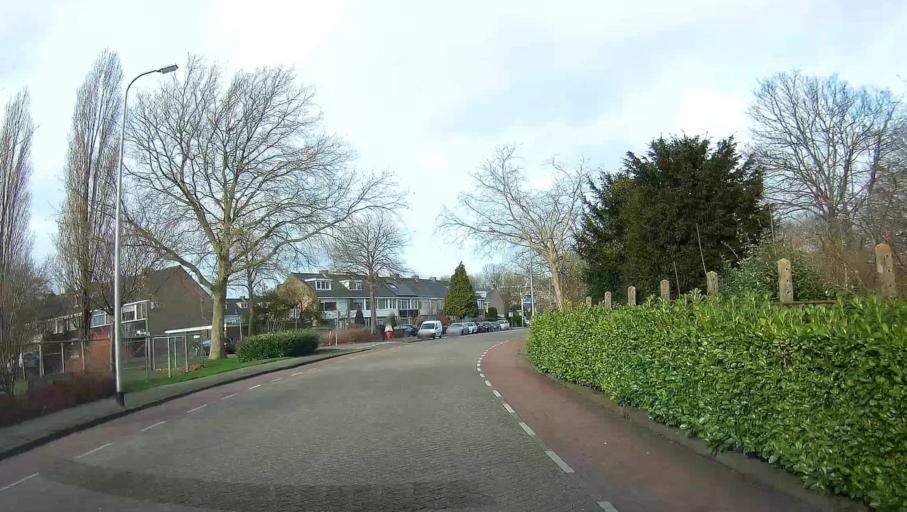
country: NL
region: South Holland
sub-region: Gemeente Ridderkerk
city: Ridderkerk
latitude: 51.8687
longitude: 4.5972
